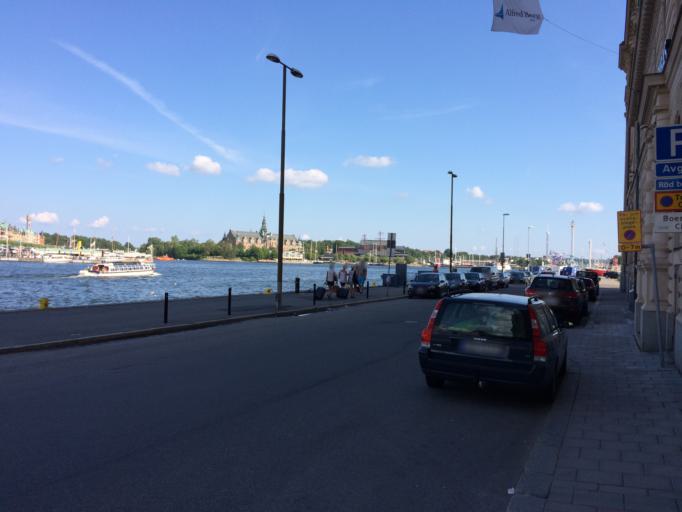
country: SE
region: Stockholm
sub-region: Stockholms Kommun
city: OEstermalm
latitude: 59.3306
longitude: 18.0779
